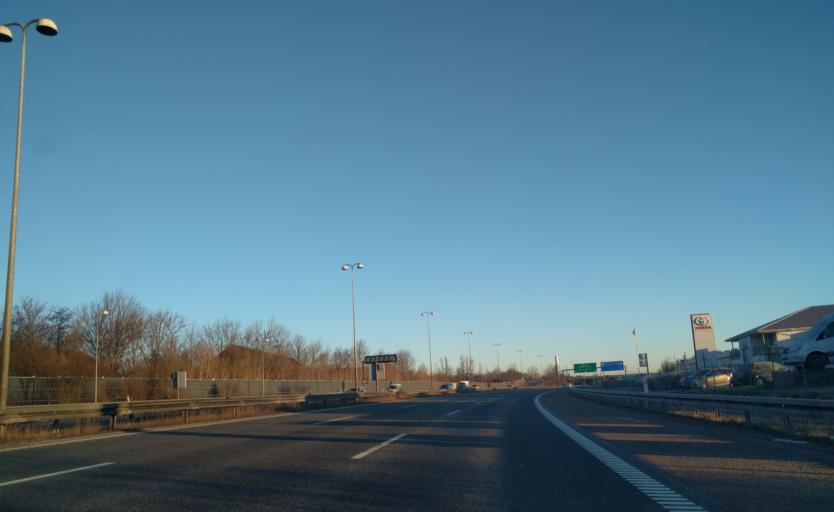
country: DK
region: North Denmark
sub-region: Alborg Kommune
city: Aalborg
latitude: 57.0655
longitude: 9.9493
